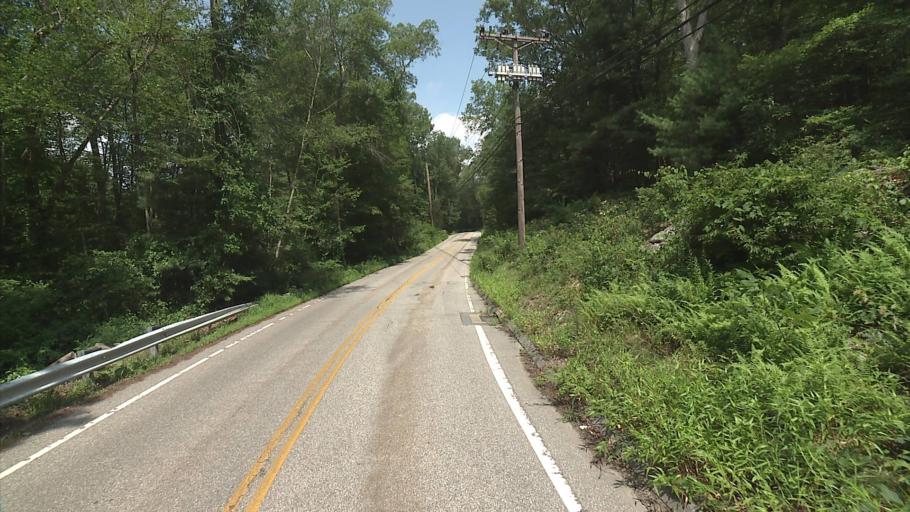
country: US
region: Connecticut
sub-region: New London County
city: Lisbon
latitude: 41.6079
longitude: -72.0217
